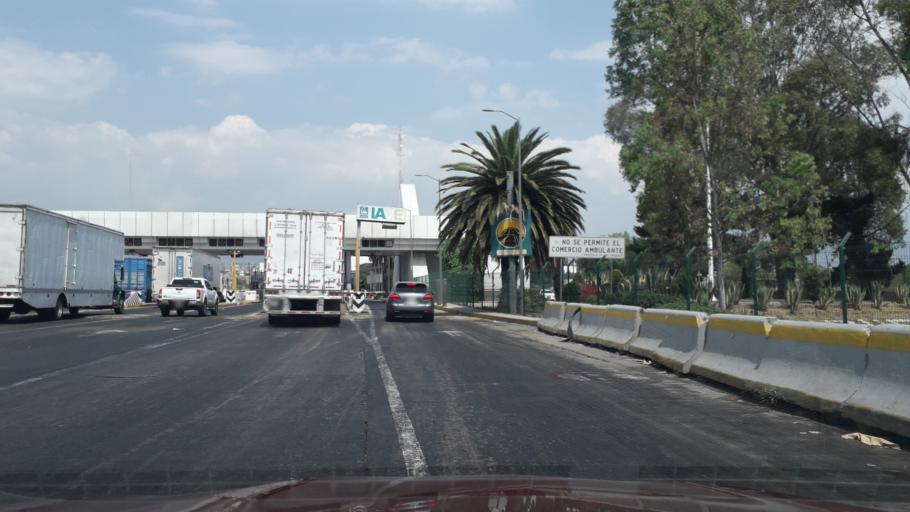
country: MX
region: Mexico
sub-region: Ixtapaluca
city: San Buenaventura
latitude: 19.2959
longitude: -98.8714
